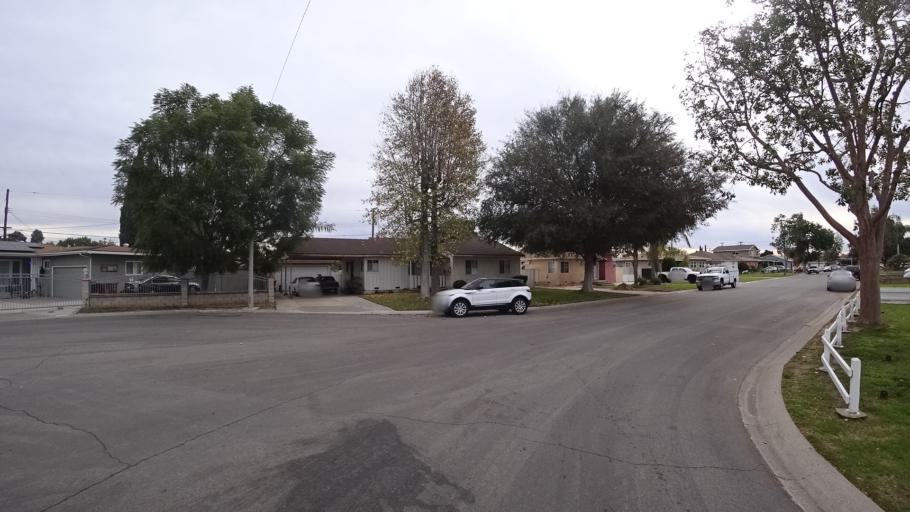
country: US
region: California
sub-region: Orange County
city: Garden Grove
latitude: 33.7722
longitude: -117.9301
